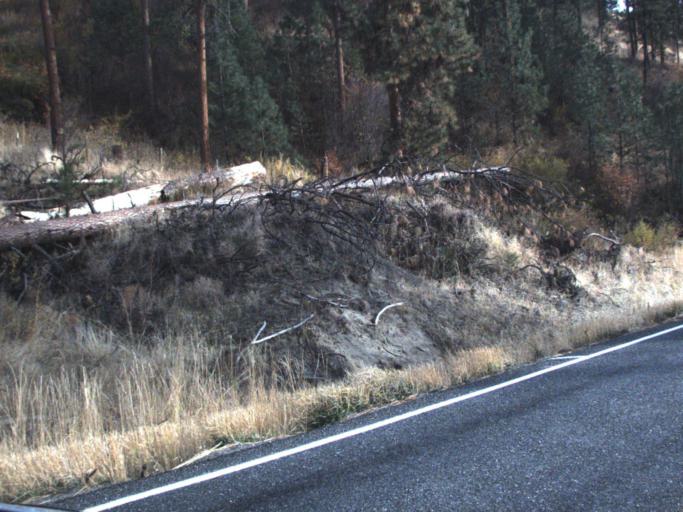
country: US
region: Washington
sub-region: Stevens County
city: Kettle Falls
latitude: 48.3344
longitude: -118.1560
